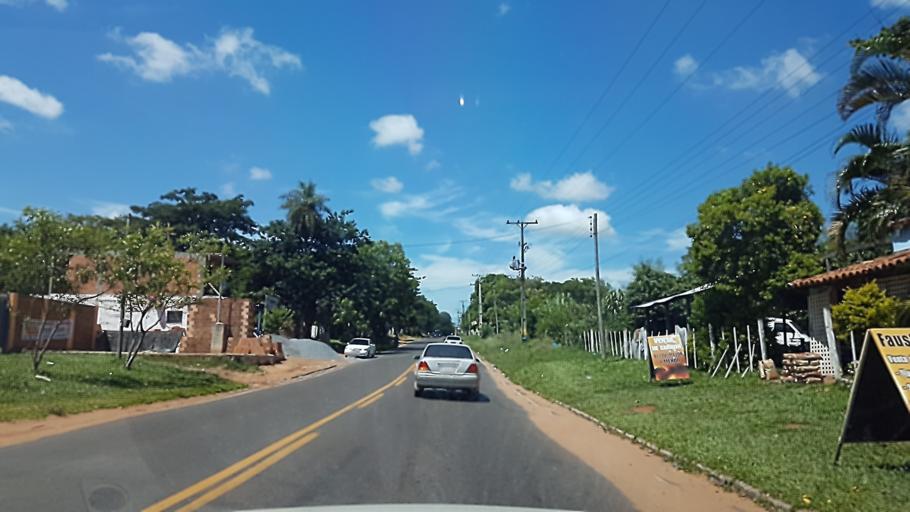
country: PY
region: Central
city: Capiata
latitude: -25.3025
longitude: -57.4646
